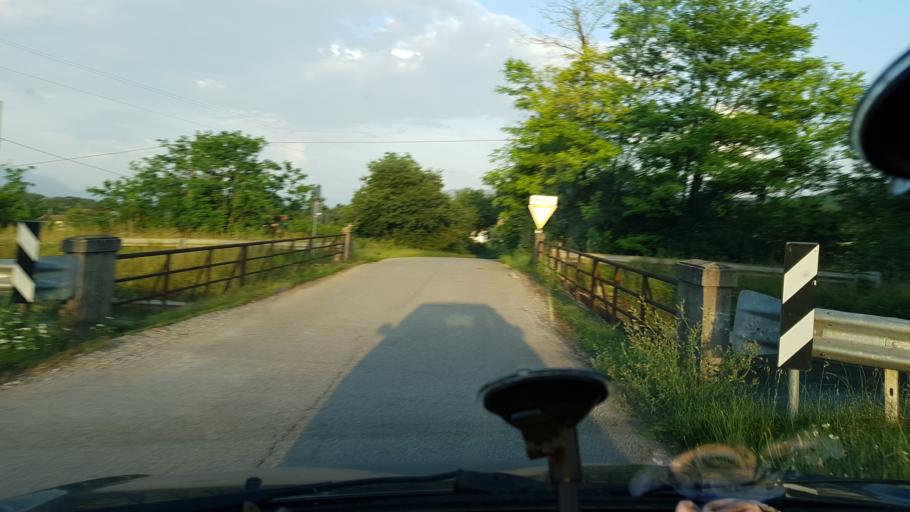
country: IT
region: Friuli Venezia Giulia
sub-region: Provincia di Gorizia
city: Mossa
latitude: 45.9095
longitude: 13.5513
